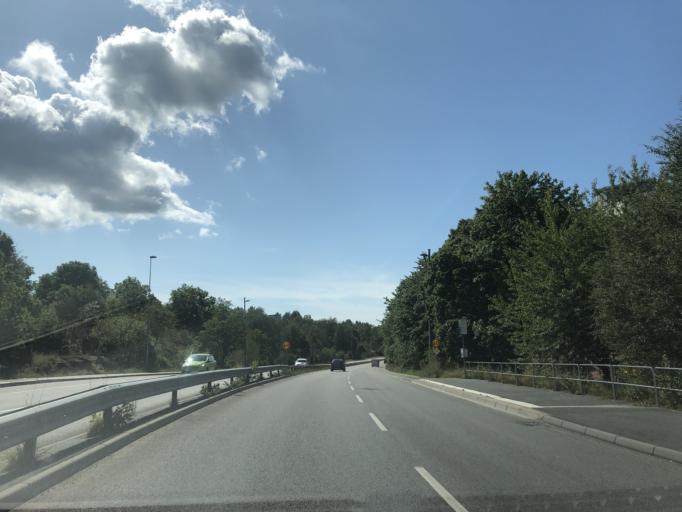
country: SE
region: Vaestra Goetaland
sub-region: Goteborg
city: Majorna
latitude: 57.7125
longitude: 11.8965
